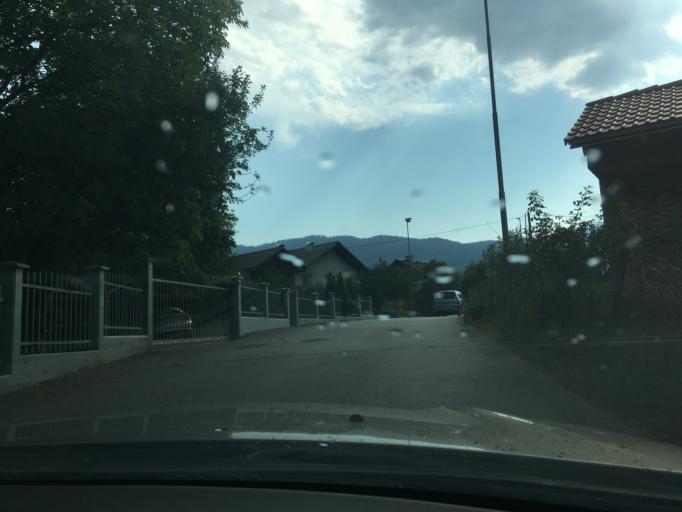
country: SI
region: Kocevje
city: Kocevje
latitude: 45.6451
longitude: 14.8701
